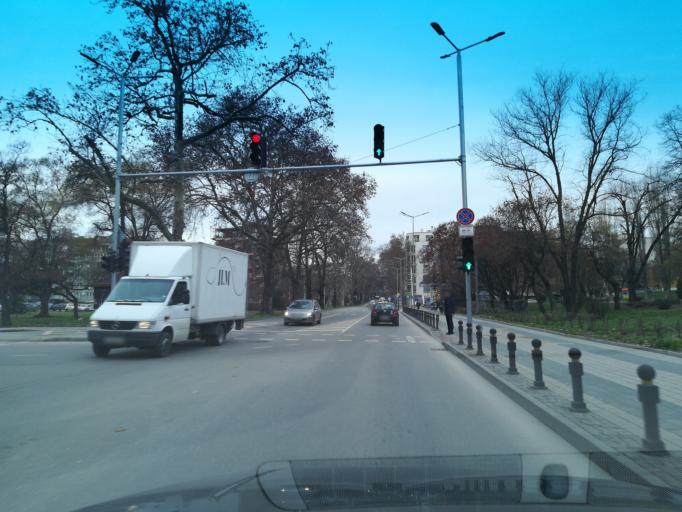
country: BG
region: Plovdiv
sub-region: Obshtina Plovdiv
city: Plovdiv
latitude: 42.1433
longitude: 24.7327
